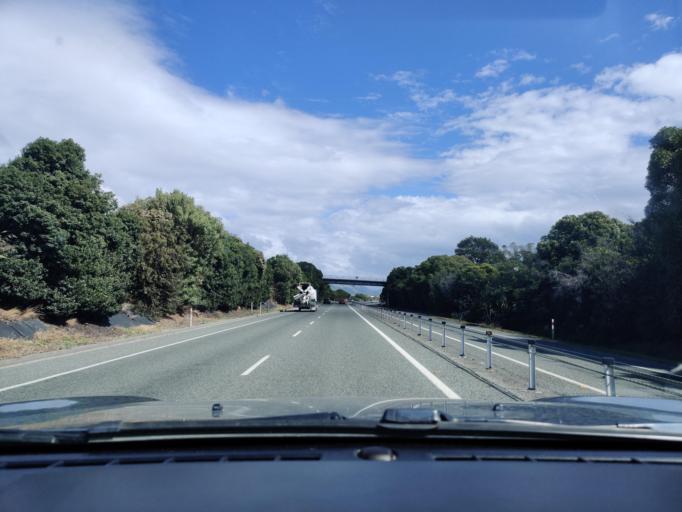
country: NZ
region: Tasman
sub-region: Tasman District
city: Richmond
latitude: -41.3058
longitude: 173.2225
